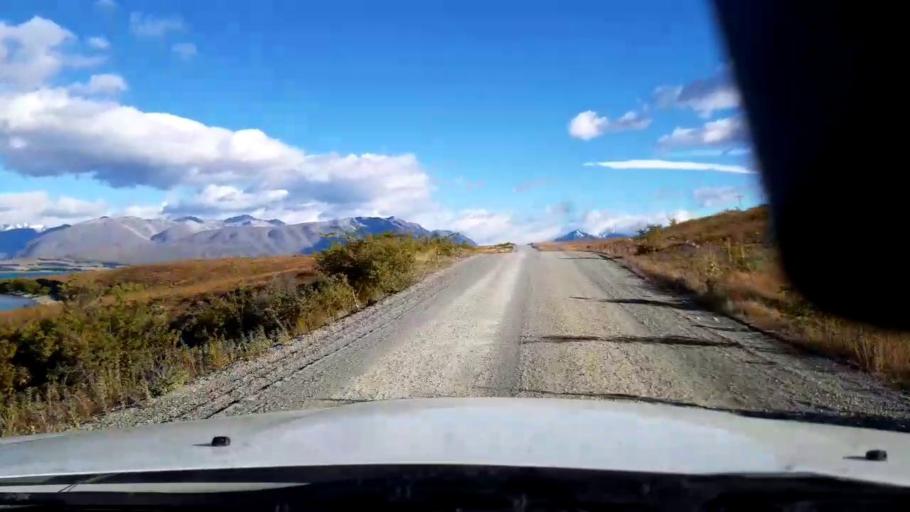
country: NZ
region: Canterbury
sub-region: Timaru District
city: Pleasant Point
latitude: -43.9251
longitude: 170.5601
